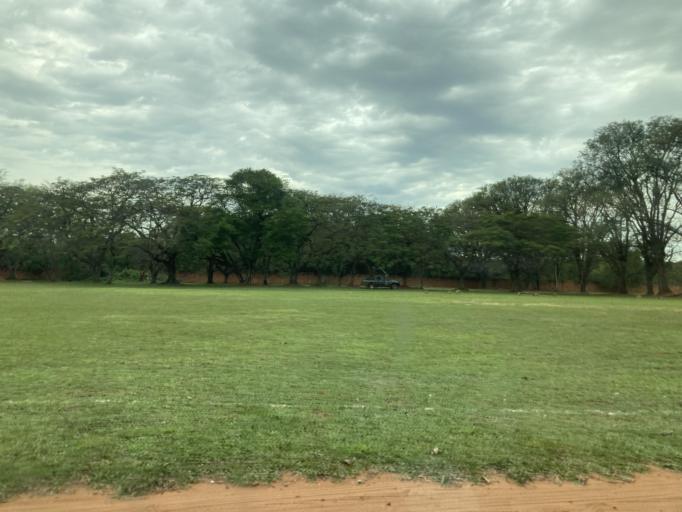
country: PY
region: Central
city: Fernando de la Mora
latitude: -25.3421
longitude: -57.5295
